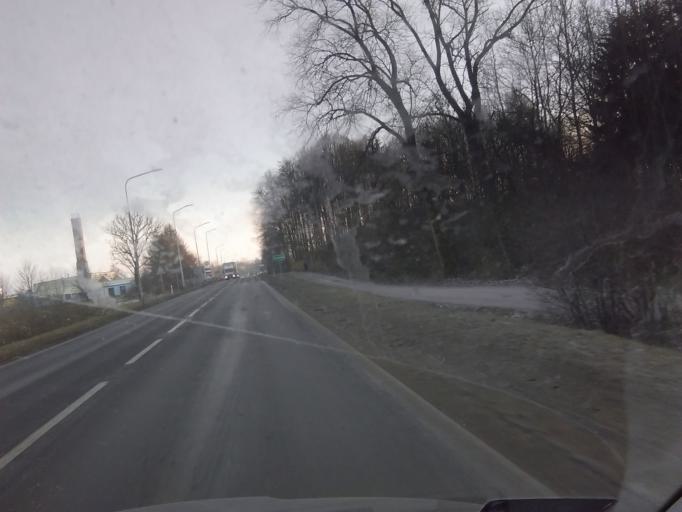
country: PL
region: West Pomeranian Voivodeship
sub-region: Powiat szczecinecki
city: Szczecinek
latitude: 53.7255
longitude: 16.6763
